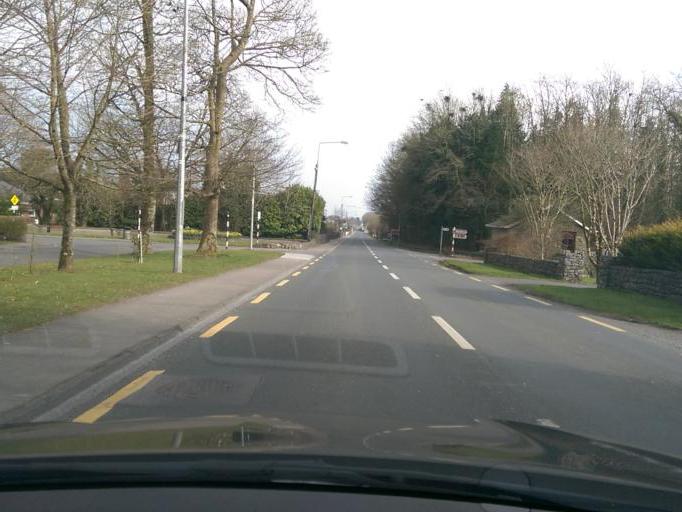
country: IE
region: Connaught
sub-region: County Galway
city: Loughrea
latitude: 53.4722
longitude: -8.5102
